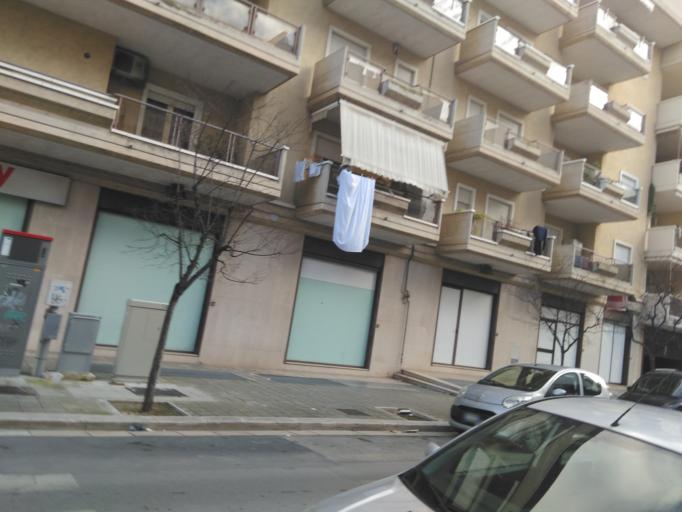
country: IT
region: Apulia
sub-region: Provincia di Barletta - Andria - Trani
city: Andria
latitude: 41.2204
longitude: 16.2999
